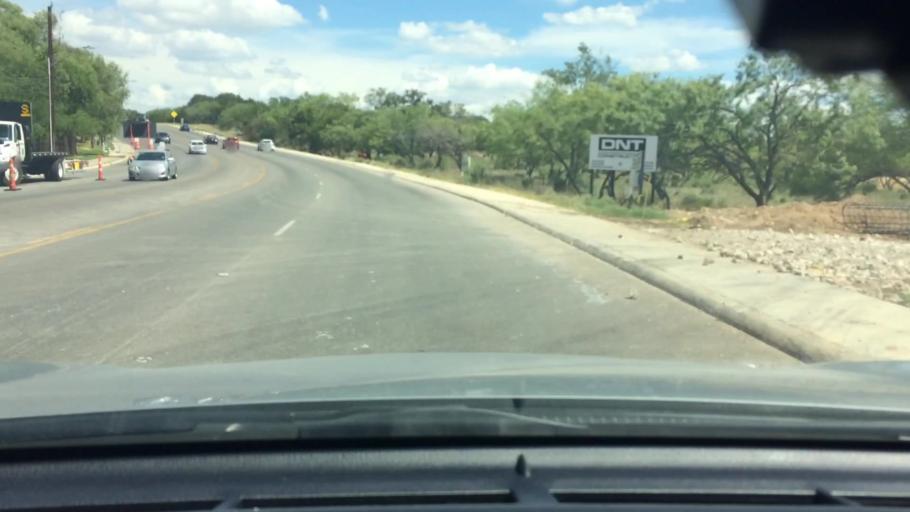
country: US
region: Texas
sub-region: Bexar County
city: Shavano Park
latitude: 29.5758
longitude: -98.6010
